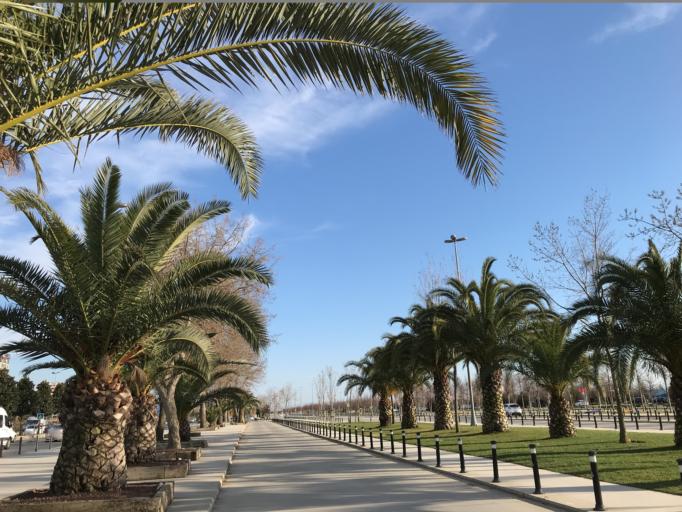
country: TR
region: Istanbul
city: Maltepe
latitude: 40.9306
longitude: 29.1189
